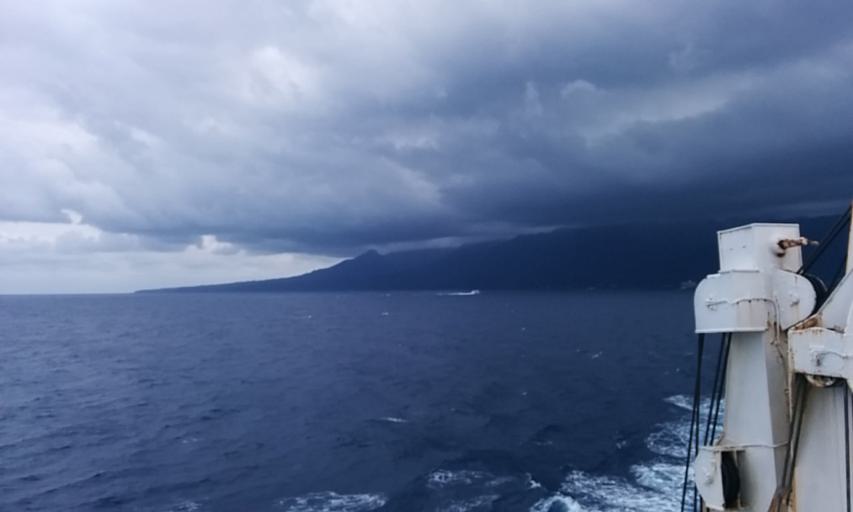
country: JP
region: Kagoshima
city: Nishinoomote
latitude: 30.4591
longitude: 130.5852
